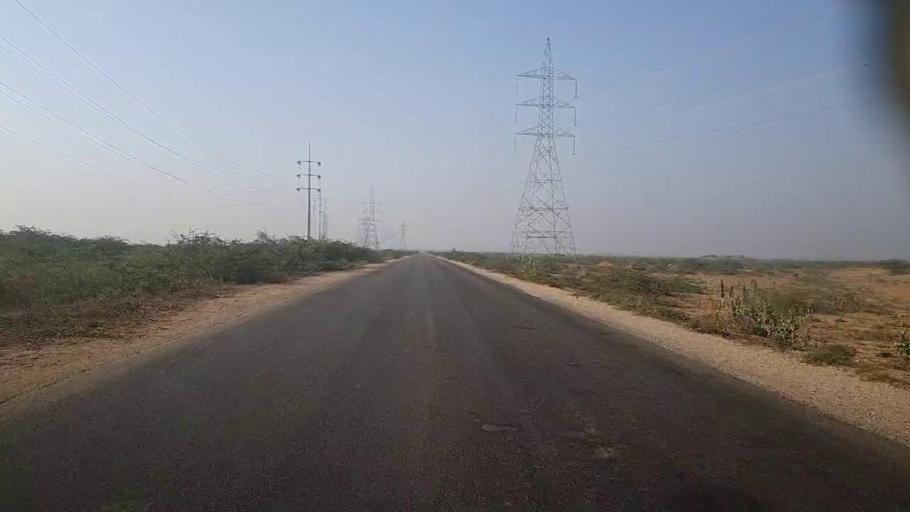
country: PK
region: Sindh
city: Gharo
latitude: 24.7665
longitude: 67.5479
